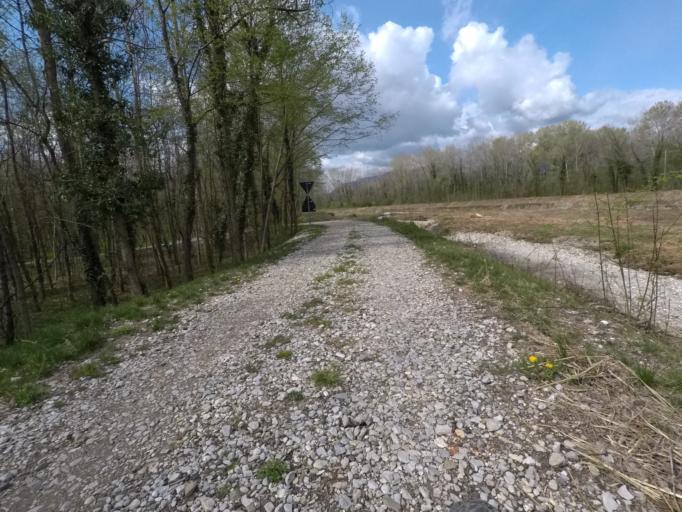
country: IT
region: Friuli Venezia Giulia
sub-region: Provincia di Udine
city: Gemona
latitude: 46.2548
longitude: 13.1278
